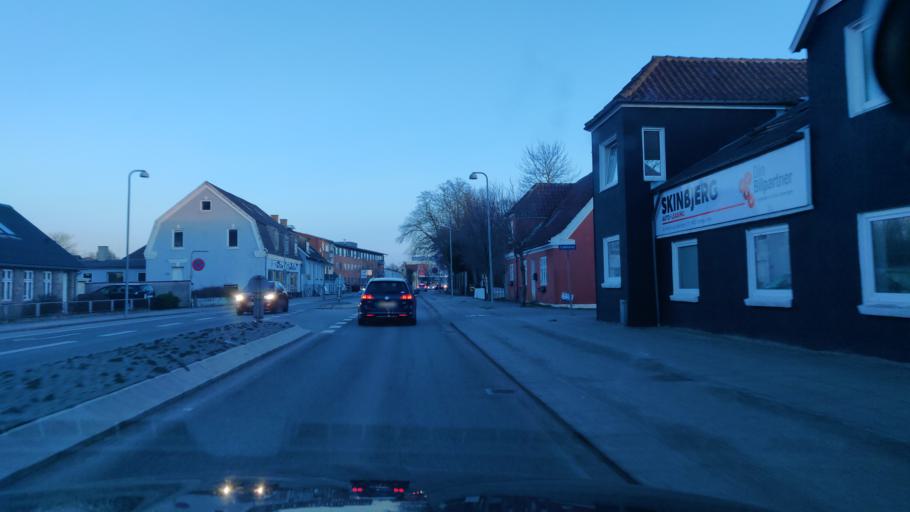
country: DK
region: North Denmark
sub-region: Alborg Kommune
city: Aalborg
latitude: 57.0685
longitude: 9.8998
